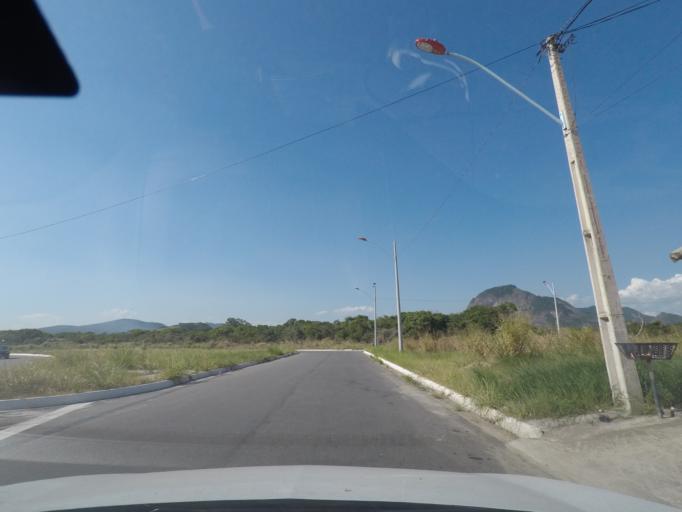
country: BR
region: Rio de Janeiro
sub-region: Marica
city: Marica
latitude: -22.9572
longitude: -42.9272
